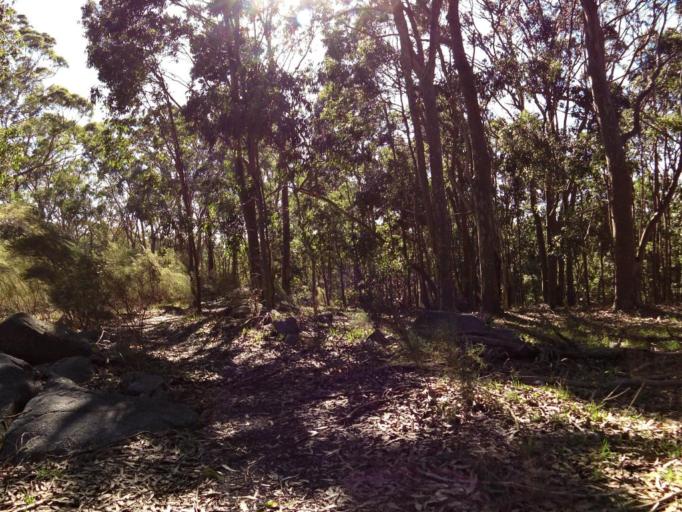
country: AU
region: Victoria
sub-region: Yarra Ranges
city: Lysterfield
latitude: -37.9428
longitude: 145.2774
